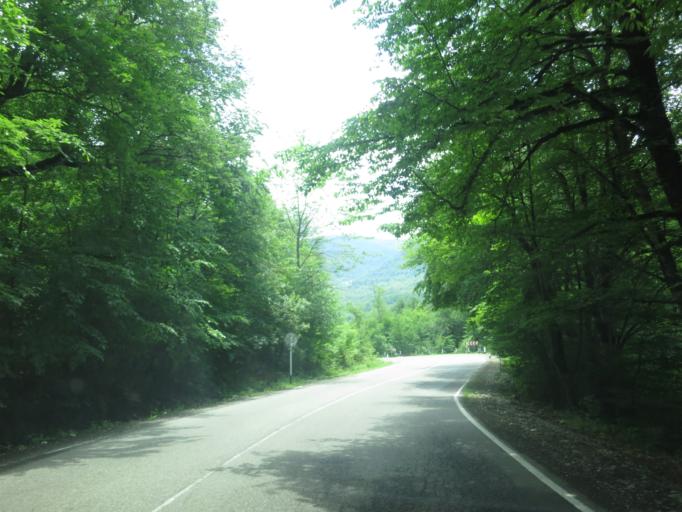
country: GE
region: Kakheti
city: Sagarejo
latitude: 41.8648
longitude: 45.3449
